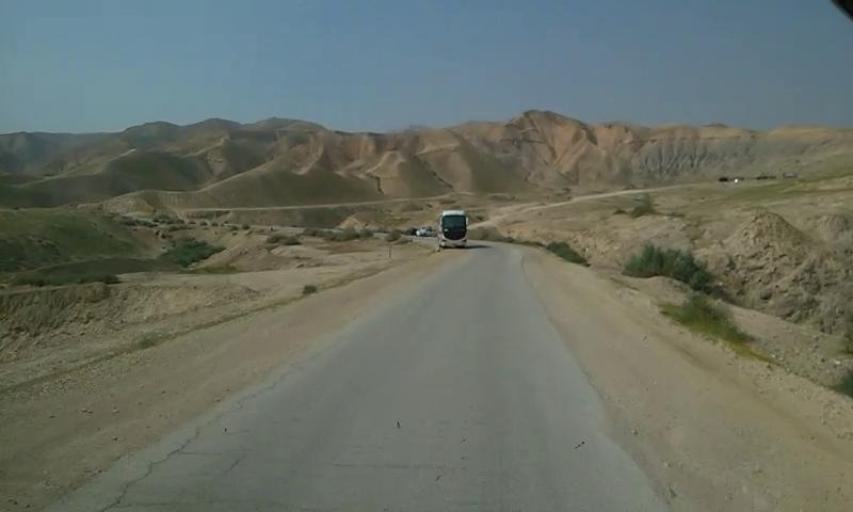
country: PS
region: West Bank
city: Jericho
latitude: 31.7804
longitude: 35.4187
